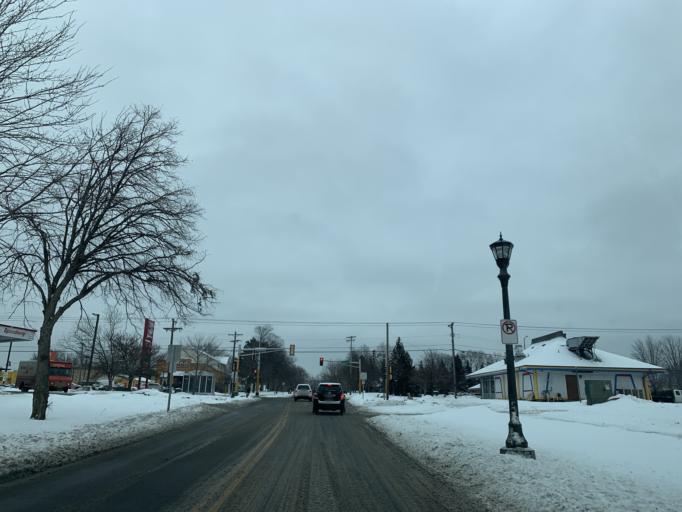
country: US
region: Minnesota
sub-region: Ramsey County
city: Little Canada
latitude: 44.9900
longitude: -93.1069
